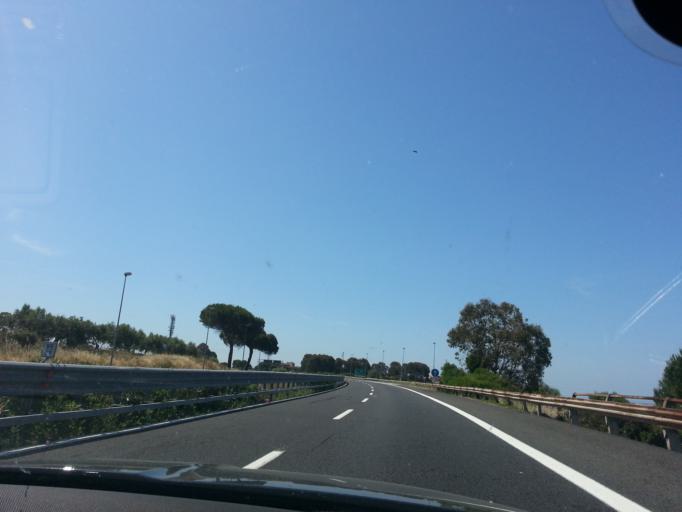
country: IT
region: Latium
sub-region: Citta metropolitana di Roma Capitale
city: Civitavecchia
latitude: 42.1076
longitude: 11.8263
